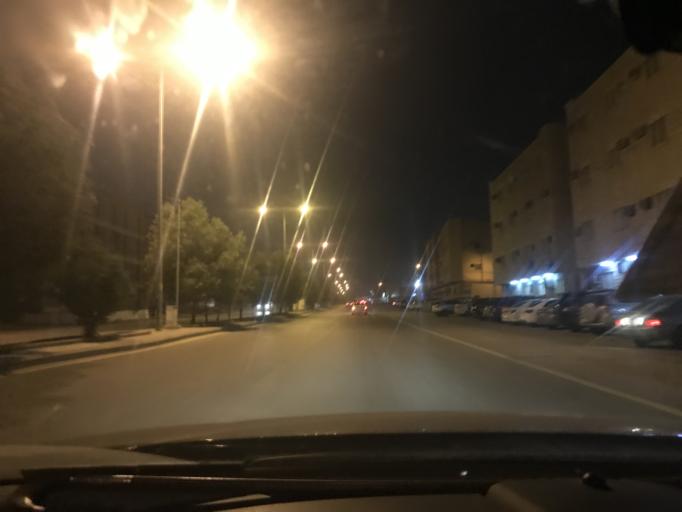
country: SA
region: Ar Riyad
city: Riyadh
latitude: 24.7502
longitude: 46.7540
